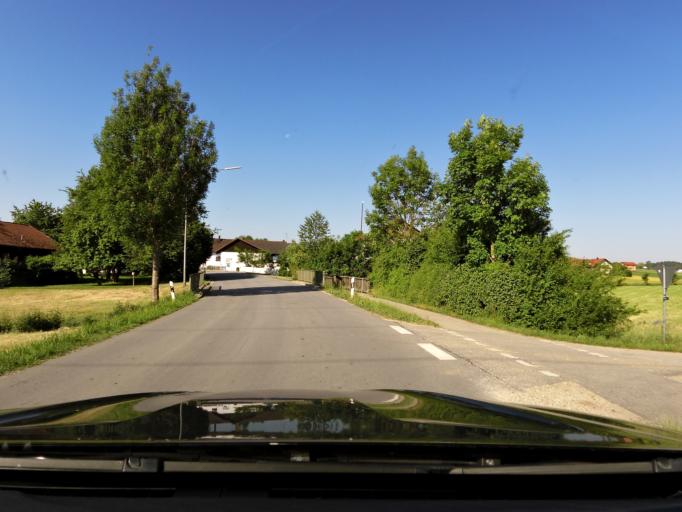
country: DE
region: Bavaria
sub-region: Upper Bavaria
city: Egglkofen
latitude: 48.4293
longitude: 12.4181
